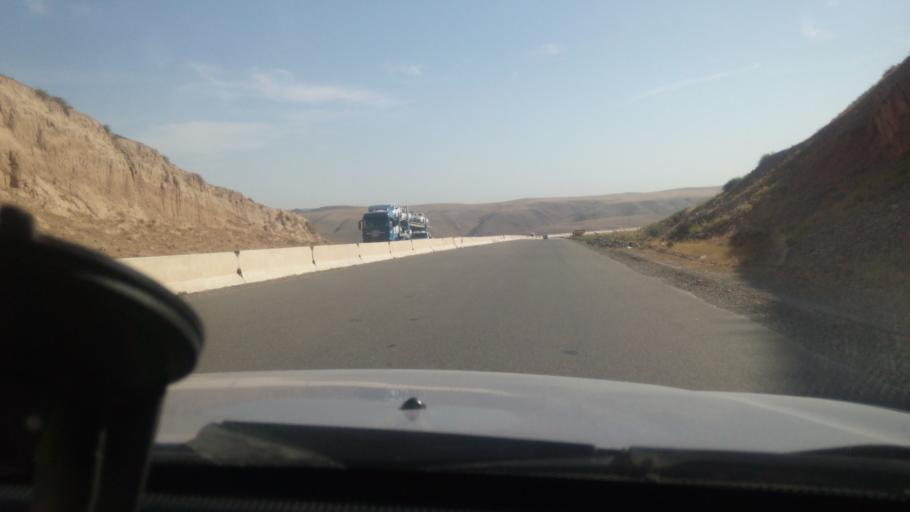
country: UZ
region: Jizzax
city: Jizzax
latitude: 40.0508
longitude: 67.6817
